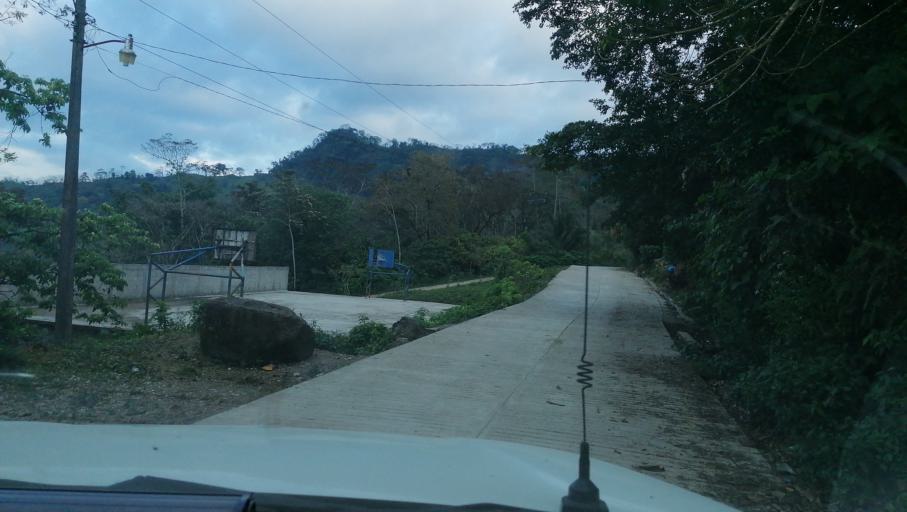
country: MX
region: Chiapas
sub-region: Francisco Leon
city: San Miguel la Sardina
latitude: 17.3114
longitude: -93.2673
